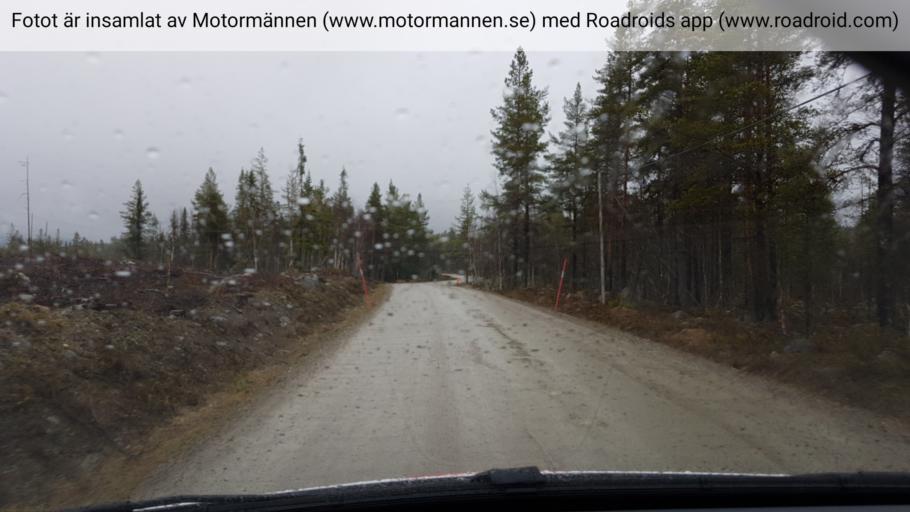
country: SE
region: Jaemtland
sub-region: Are Kommun
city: Jarpen
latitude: 62.4990
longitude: 13.5012
